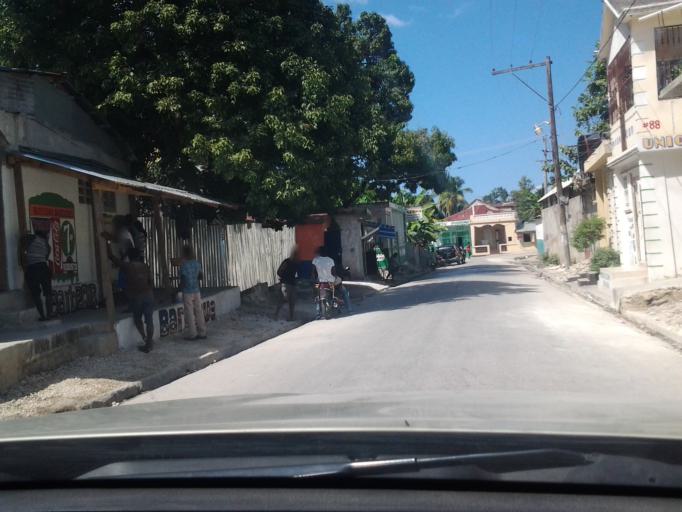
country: HT
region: Ouest
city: Tigwav
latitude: 18.4334
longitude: -72.8639
